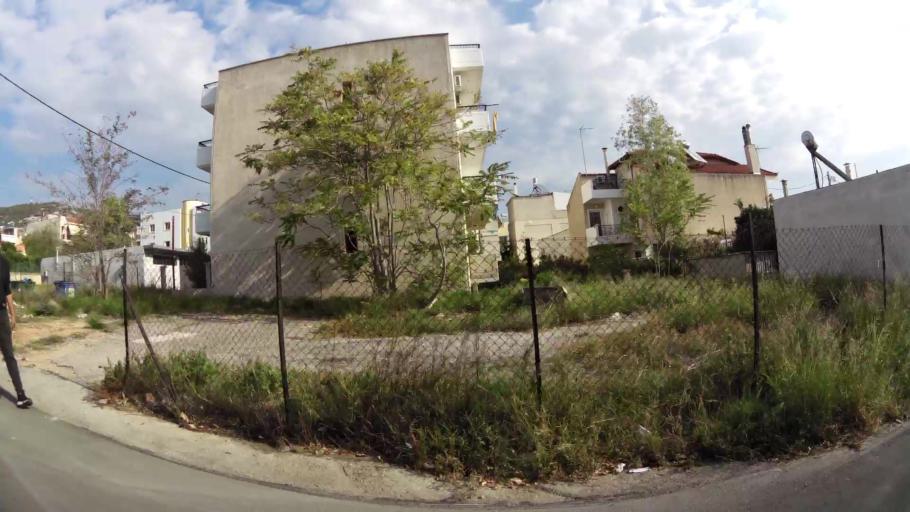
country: GR
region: Attica
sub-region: Nomarchia Athinas
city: Kamateron
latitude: 38.0526
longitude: 23.6972
